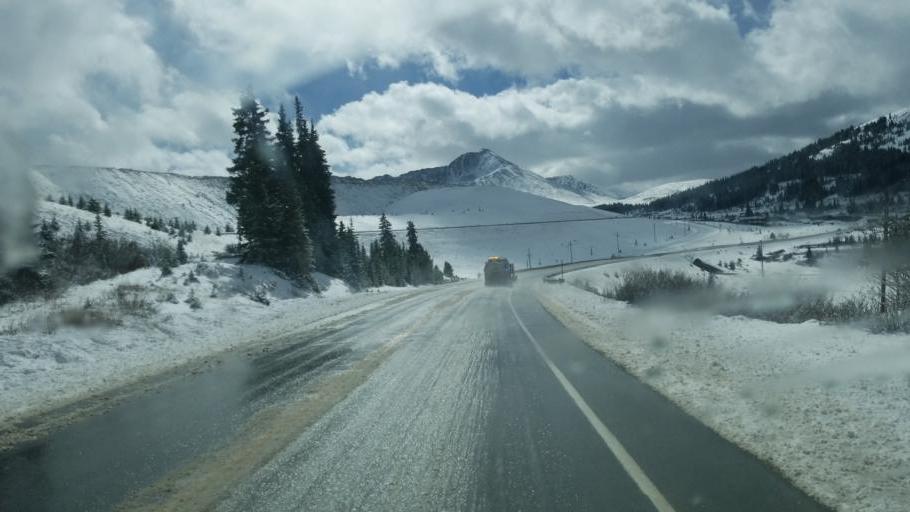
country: US
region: Colorado
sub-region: Lake County
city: Leadville
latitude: 39.3841
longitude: -106.1908
